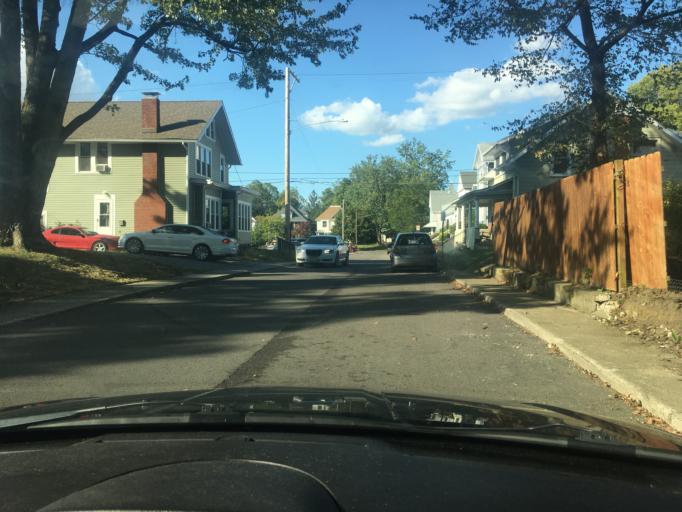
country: US
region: Ohio
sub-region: Logan County
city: Bellefontaine
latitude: 40.3597
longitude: -83.7542
